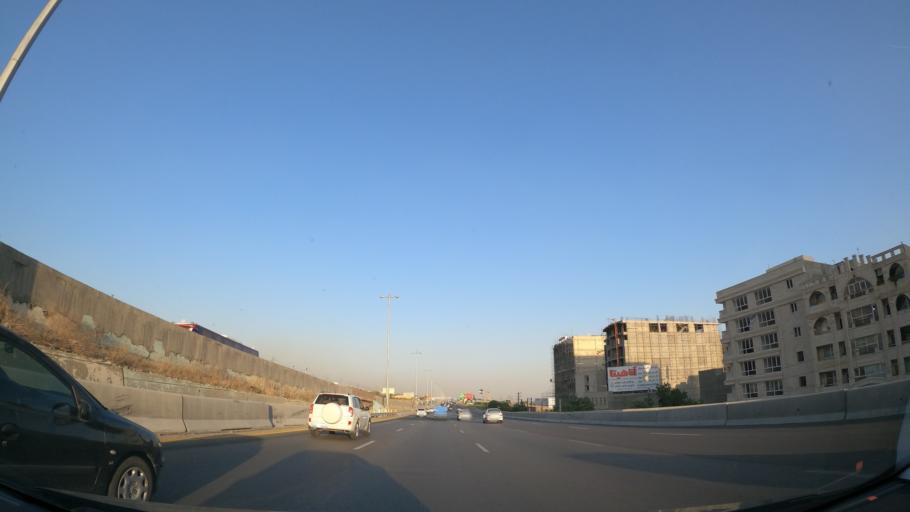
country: IR
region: Tehran
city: Shahr-e Qods
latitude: 35.7564
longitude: 51.0710
